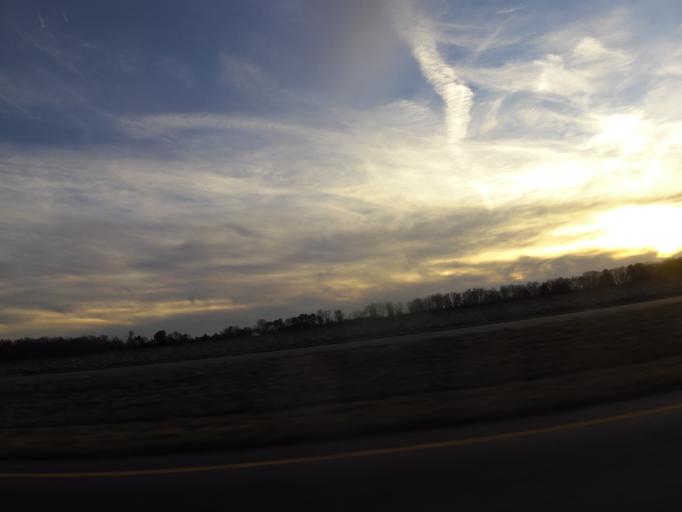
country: US
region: Virginia
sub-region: City of Franklin
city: Franklin
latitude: 36.6879
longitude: -76.9762
